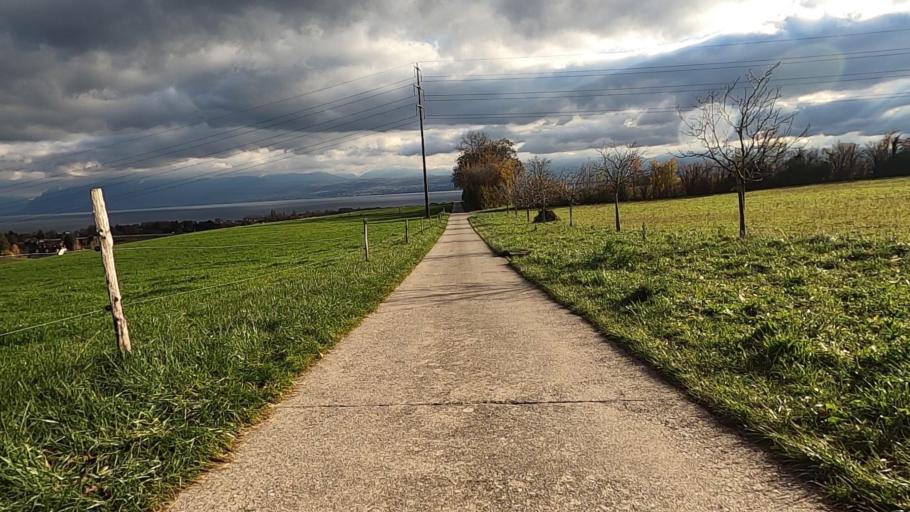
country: CH
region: Vaud
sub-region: Morges District
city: Saint-Prex
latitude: 46.5117
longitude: 6.4568
